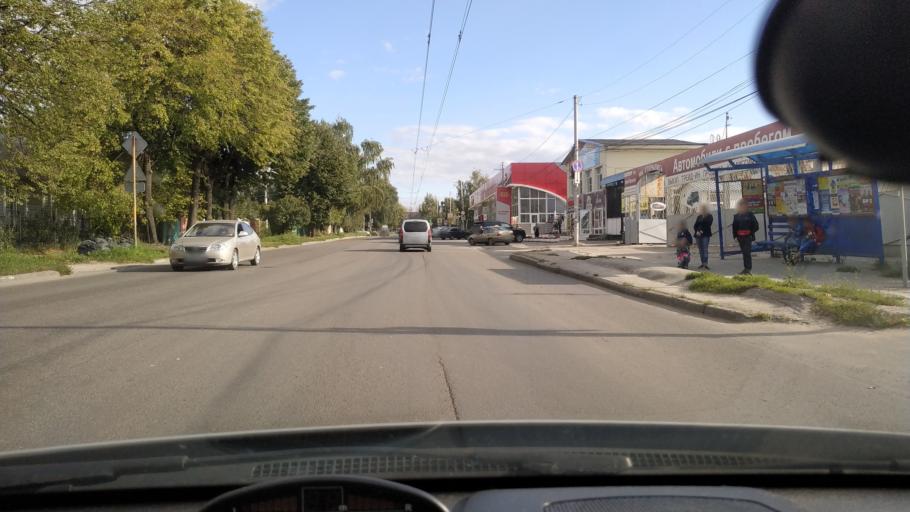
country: RU
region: Rjazan
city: Ryazan'
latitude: 54.6127
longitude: 39.6962
